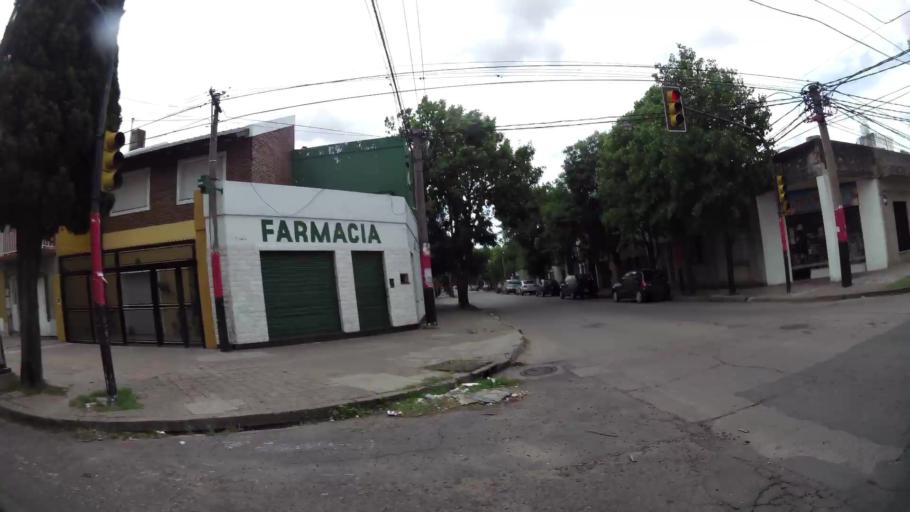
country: AR
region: Santa Fe
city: Gobernador Galvez
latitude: -33.0000
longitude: -60.6535
